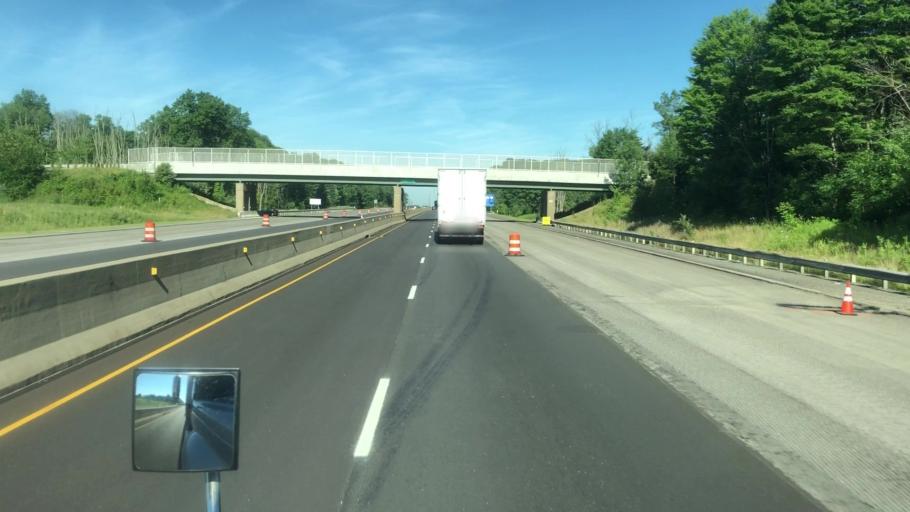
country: US
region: Ohio
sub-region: Portage County
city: Hiram
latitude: 41.2435
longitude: -81.1604
